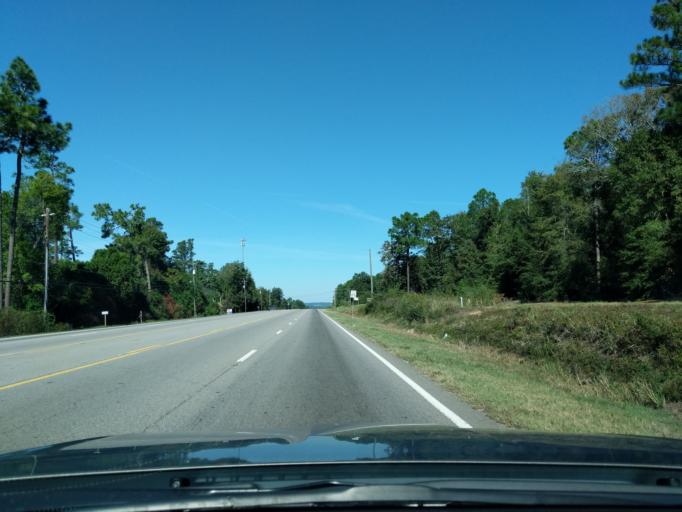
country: US
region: Georgia
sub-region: Richmond County
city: Augusta
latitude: 33.3740
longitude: -81.9993
